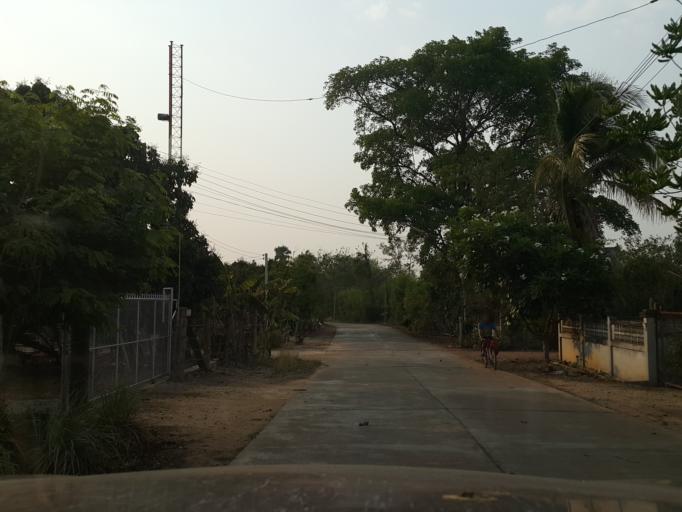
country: TH
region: Lamphun
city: Li
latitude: 17.8087
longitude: 98.9490
